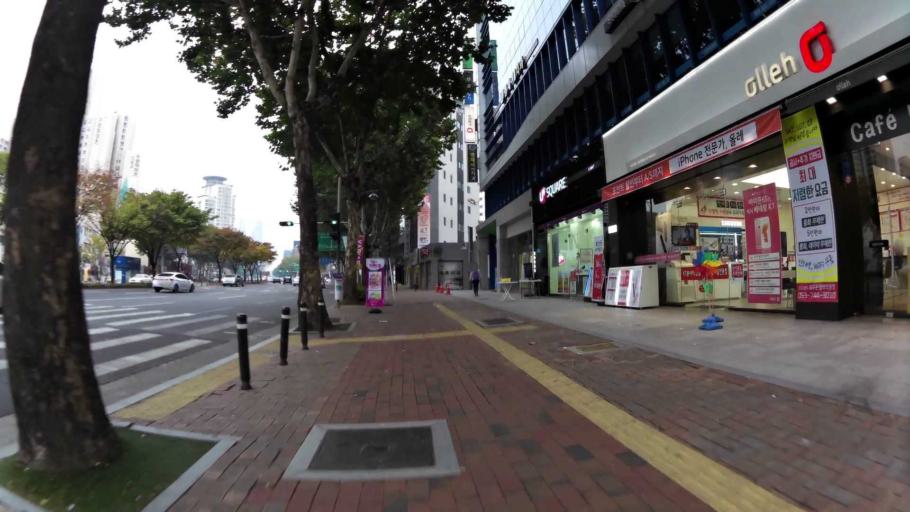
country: KR
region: Daegu
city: Daegu
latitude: 35.8599
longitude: 128.6115
